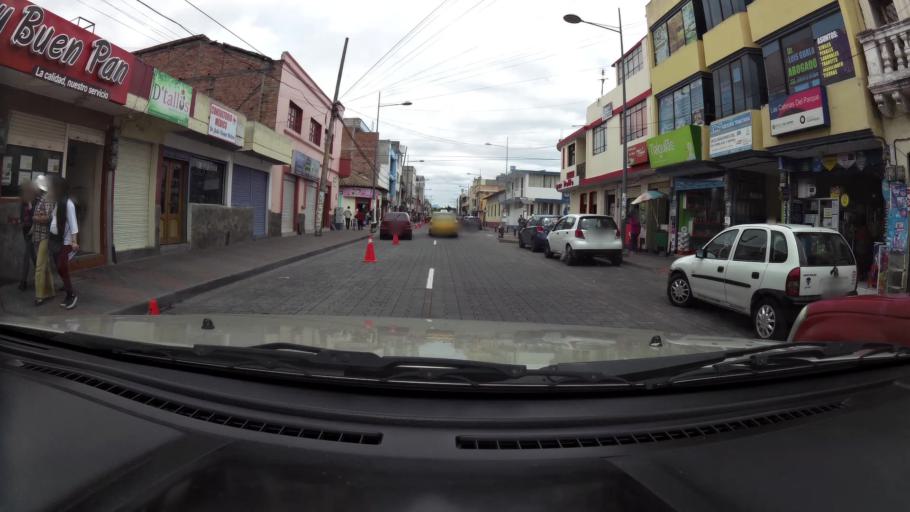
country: EC
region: Cotopaxi
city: San Miguel de Salcedo
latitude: -1.0331
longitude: -78.5909
